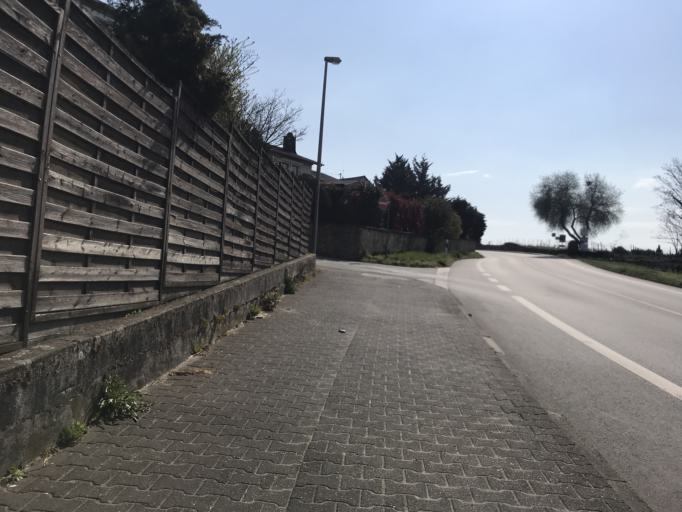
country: DE
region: Hesse
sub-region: Regierungsbezirk Darmstadt
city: Florsheim
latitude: 50.0272
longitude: 8.4014
